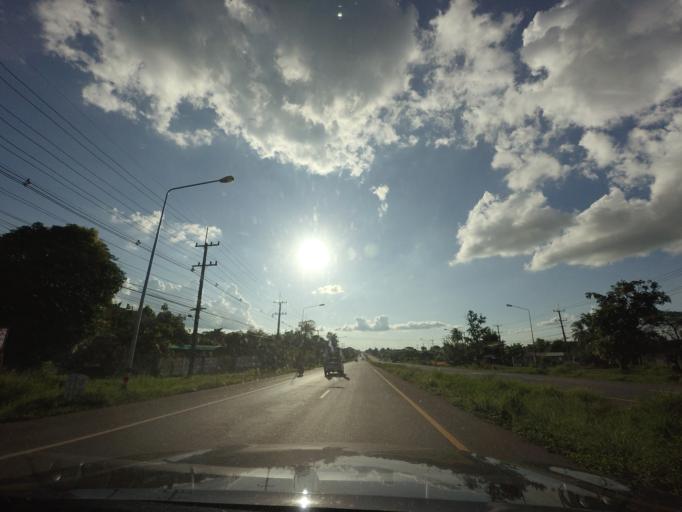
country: TH
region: Changwat Udon Thani
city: Nong Han
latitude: 17.3628
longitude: 103.1431
